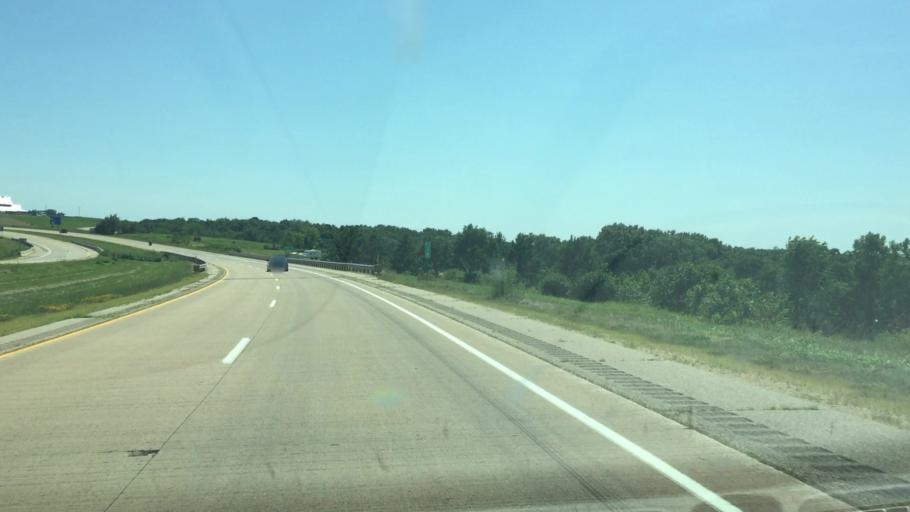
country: US
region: Wisconsin
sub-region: Iowa County
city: Mineral Point
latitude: 42.8630
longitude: -90.2018
